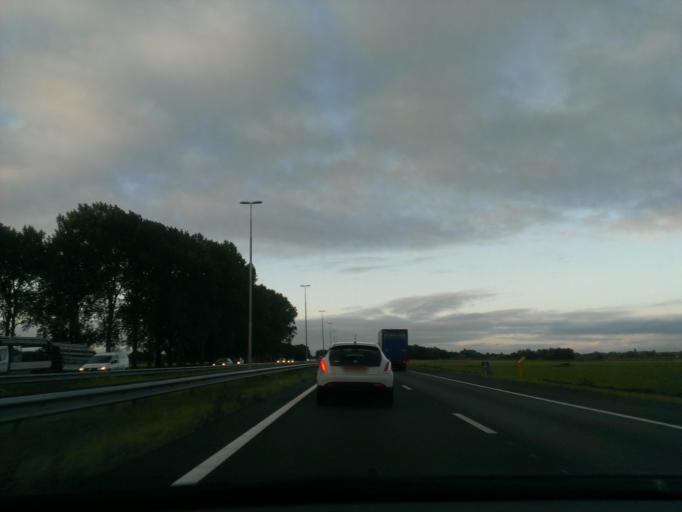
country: NL
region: Gelderland
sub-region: Gemeente Epe
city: Vaassen
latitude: 52.2753
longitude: 6.0058
